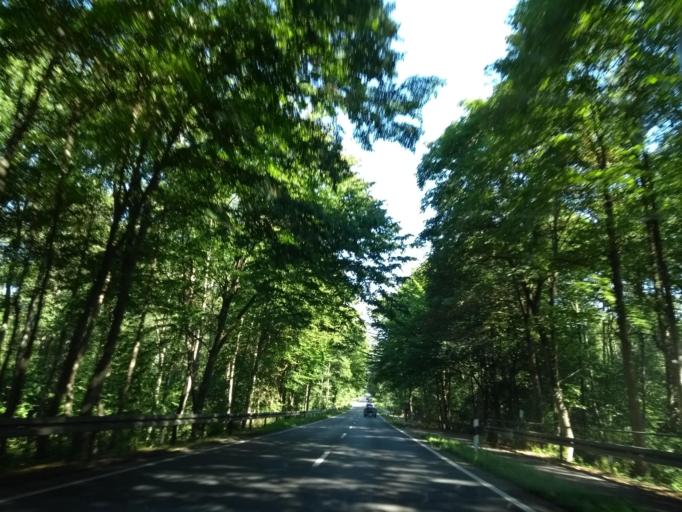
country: DE
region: Lower Saxony
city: Haste
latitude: 52.3940
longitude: 9.4005
